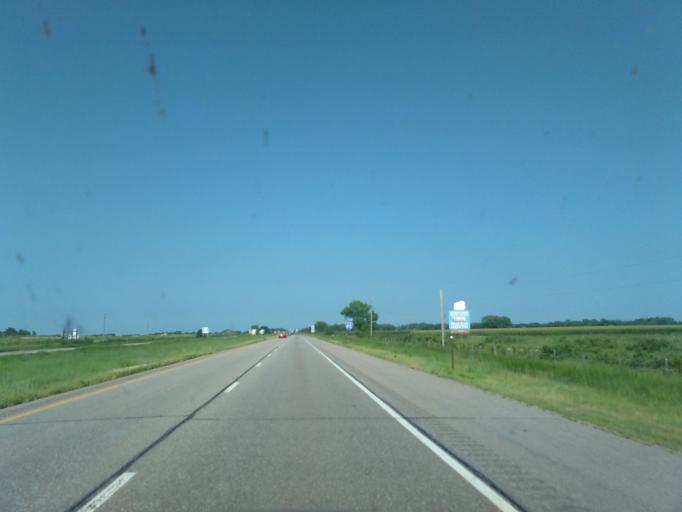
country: US
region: Nebraska
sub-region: Hall County
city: Wood River
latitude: 40.8004
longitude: -98.4865
